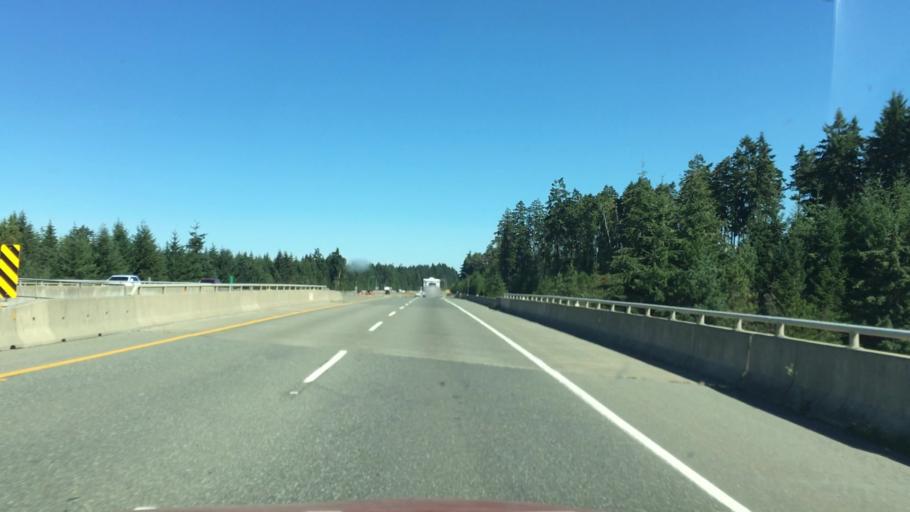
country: CA
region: British Columbia
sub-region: Regional District of Nanaimo
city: Parksville
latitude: 49.3056
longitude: -124.3263
